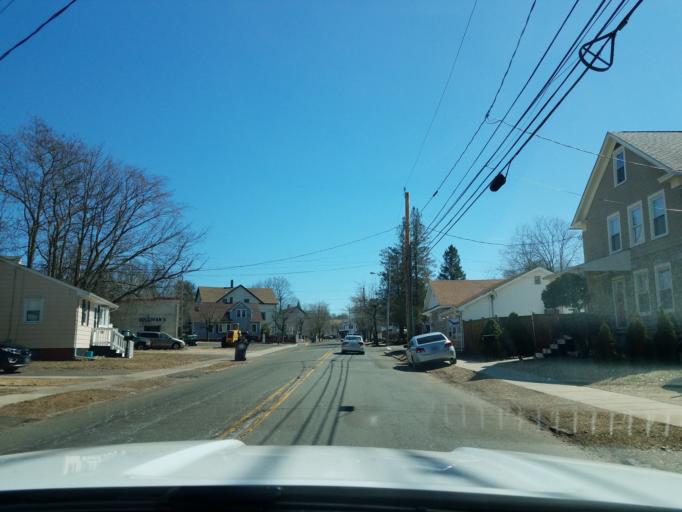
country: US
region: Connecticut
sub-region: New Haven County
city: Wallingford
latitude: 41.4551
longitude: -72.8317
